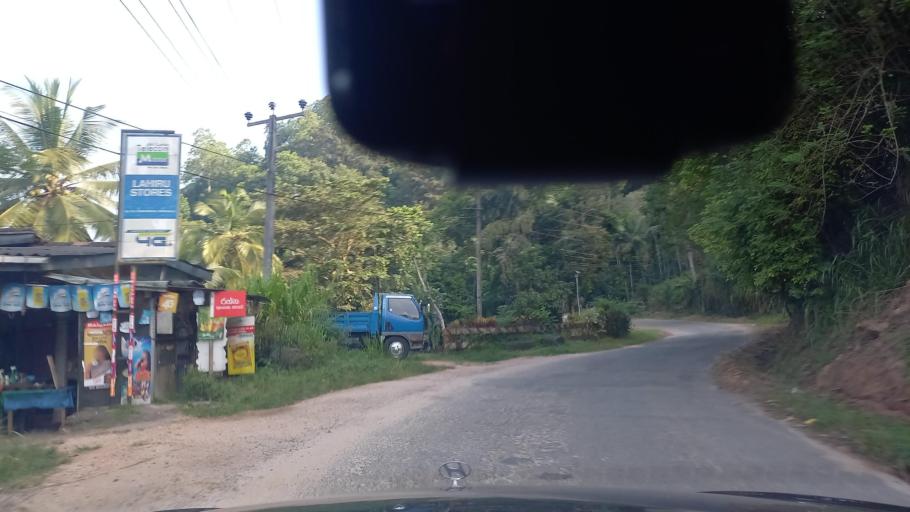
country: LK
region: Central
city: Gampola
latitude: 7.2241
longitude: 80.6051
